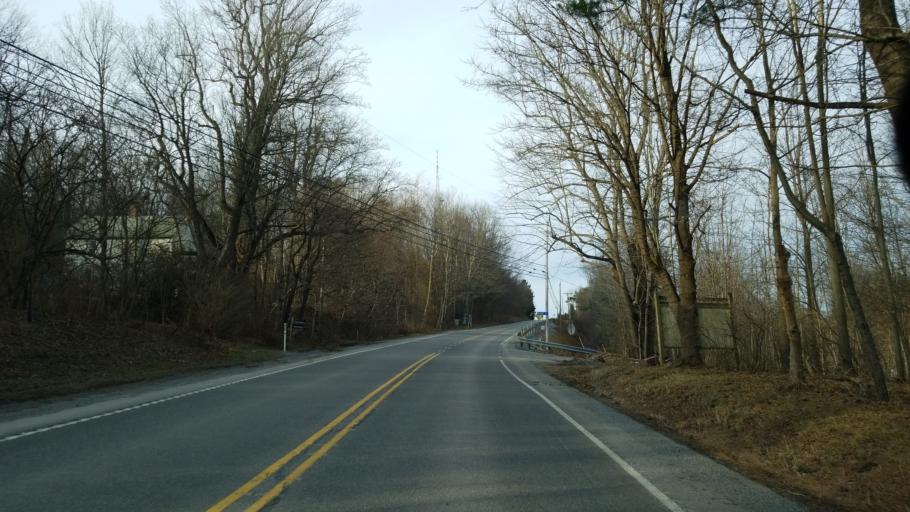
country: US
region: Pennsylvania
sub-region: Clearfield County
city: Sandy
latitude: 41.0423
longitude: -78.7008
